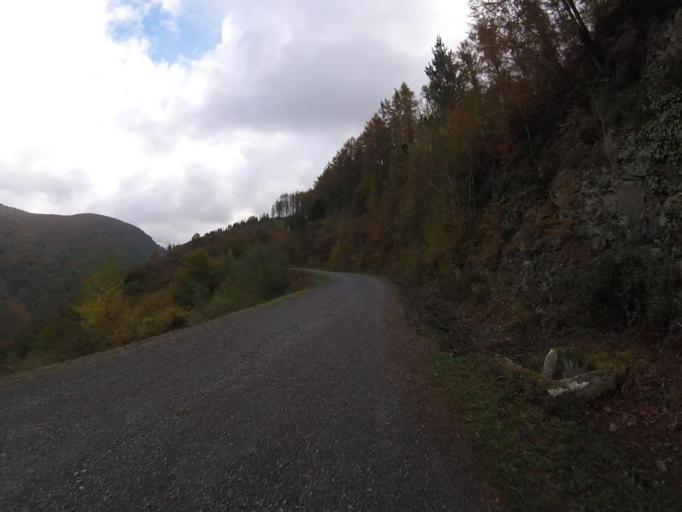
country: ES
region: Navarre
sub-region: Provincia de Navarra
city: Goizueta
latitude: 43.2256
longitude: -1.8269
